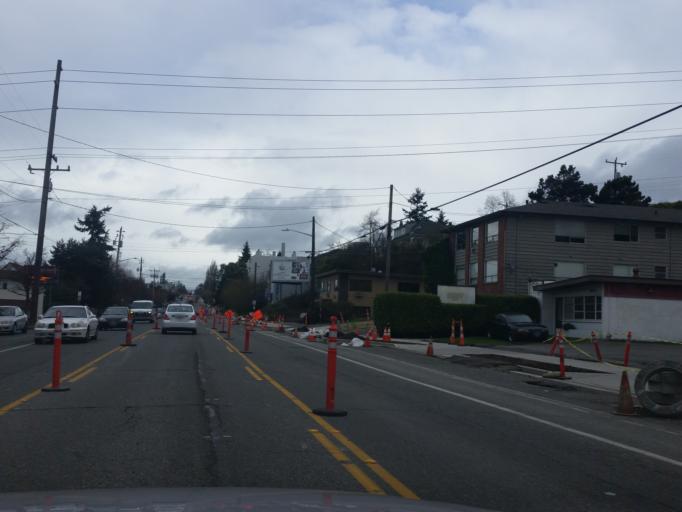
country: US
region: Washington
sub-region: King County
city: Shoreline
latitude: 47.6972
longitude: -122.3553
